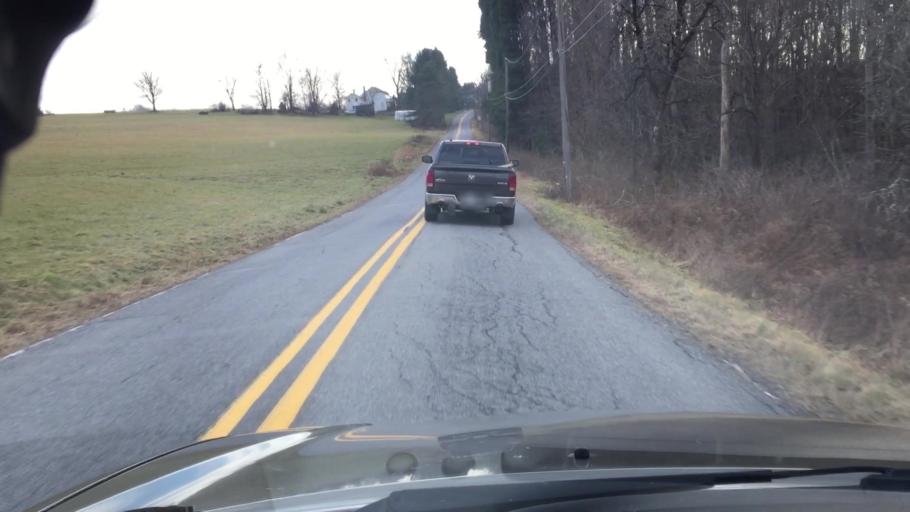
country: US
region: Pennsylvania
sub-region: Luzerne County
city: Back Mountain
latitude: 41.3219
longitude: -76.0663
